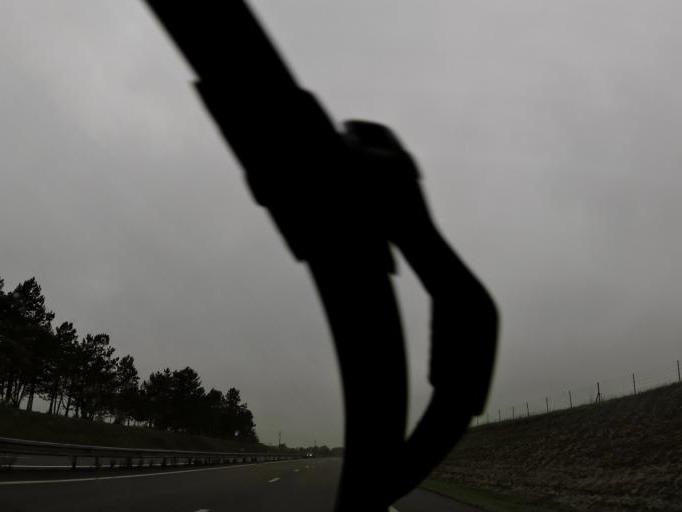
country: FR
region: Champagne-Ardenne
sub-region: Departement de la Marne
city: Fagnieres
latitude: 49.0410
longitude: 4.3313
